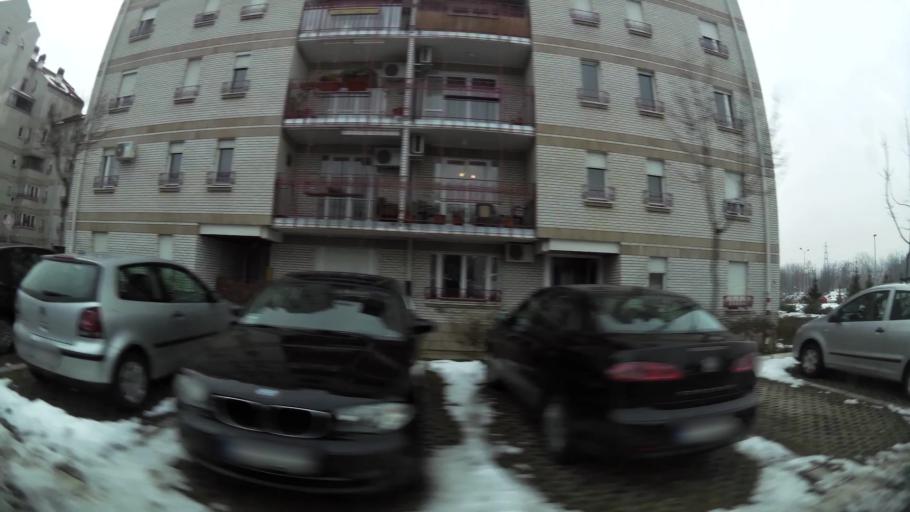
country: RS
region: Central Serbia
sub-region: Belgrade
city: Zemun
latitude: 44.8181
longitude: 20.3828
